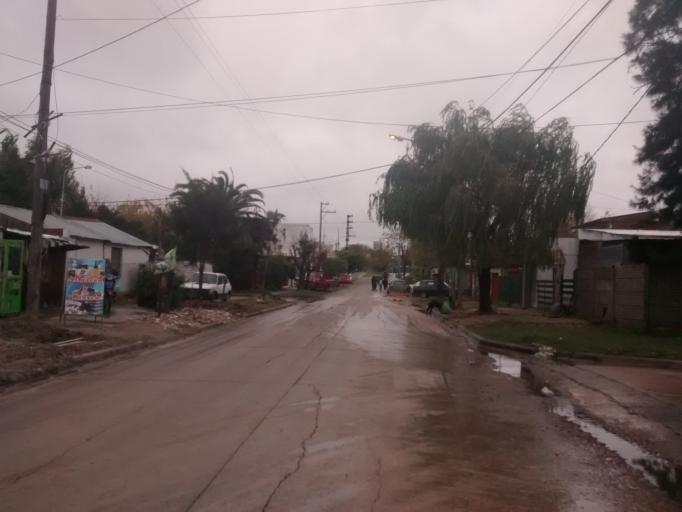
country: AR
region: Buenos Aires
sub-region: Partido de La Plata
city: La Plata
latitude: -34.8911
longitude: -57.9462
